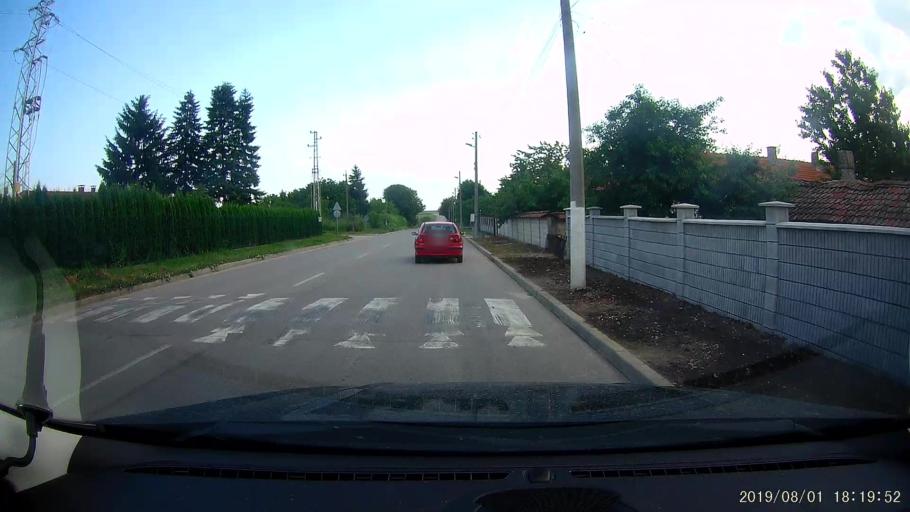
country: BG
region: Shumen
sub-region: Obshtina Kaolinovo
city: Kaolinovo
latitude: 43.6796
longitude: 27.0907
